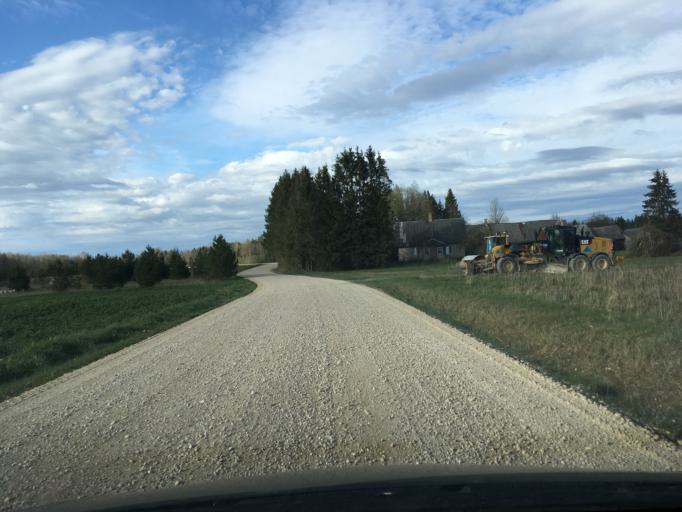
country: EE
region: Raplamaa
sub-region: Maerjamaa vald
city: Marjamaa
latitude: 58.9798
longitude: 24.3613
